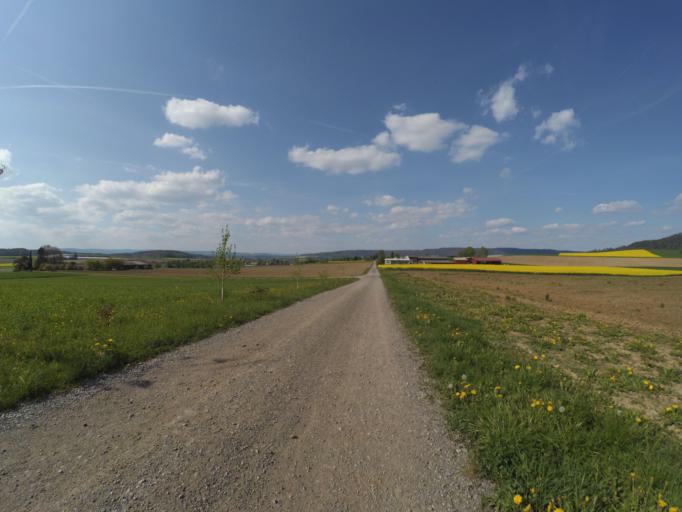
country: CH
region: Thurgau
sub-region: Frauenfeld District
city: Diessenhofen
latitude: 47.6584
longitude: 8.7523
